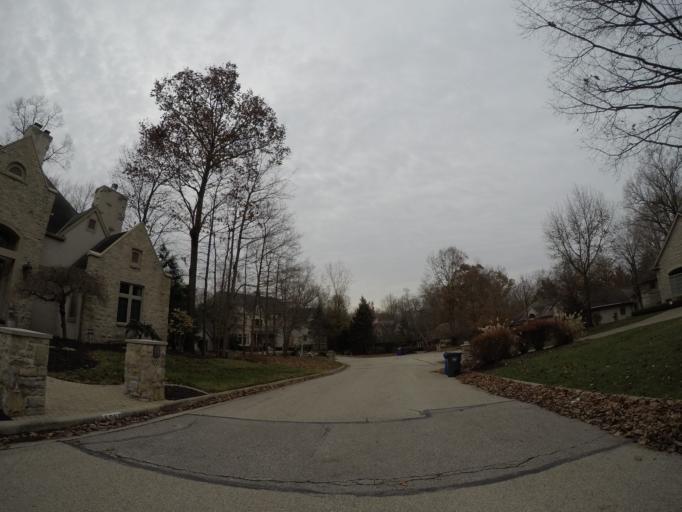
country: US
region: Ohio
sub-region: Franklin County
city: Dublin
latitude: 40.0597
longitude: -83.0875
